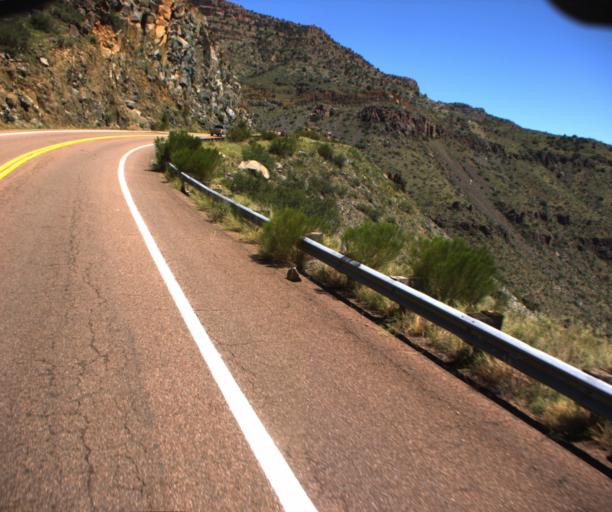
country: US
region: Arizona
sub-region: Navajo County
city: Cibecue
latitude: 33.7983
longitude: -110.4886
